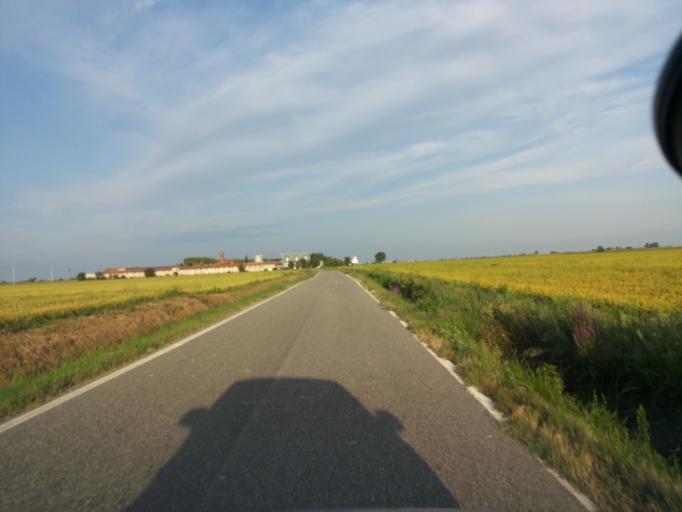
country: IT
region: Piedmont
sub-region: Provincia di Vercelli
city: Sali Vercellese
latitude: 45.3245
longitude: 8.3012
